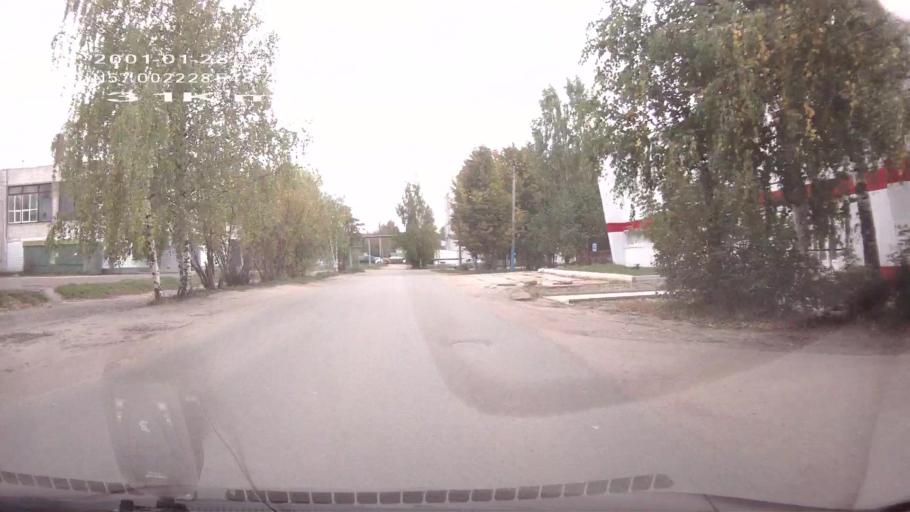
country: RU
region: Mariy-El
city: Kuzhener
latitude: 57.0019
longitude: 48.7404
